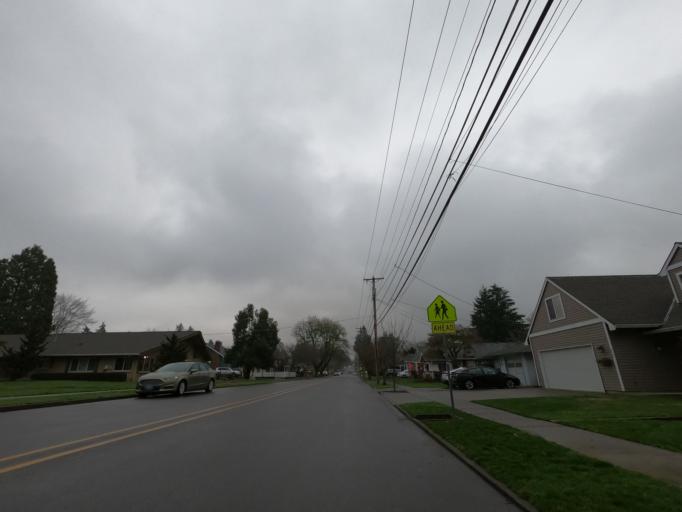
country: US
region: Oregon
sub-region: Clackamas County
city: Gladstone
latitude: 45.3834
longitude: -122.5944
